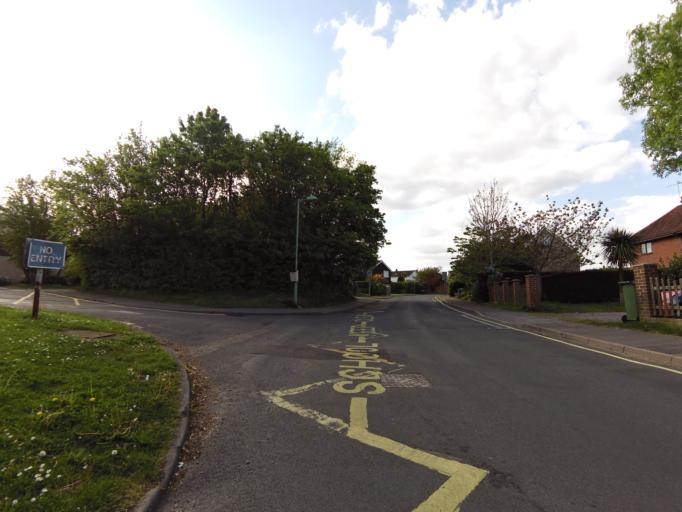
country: GB
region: England
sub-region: Suffolk
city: Beccles
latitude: 52.4493
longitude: 1.5949
